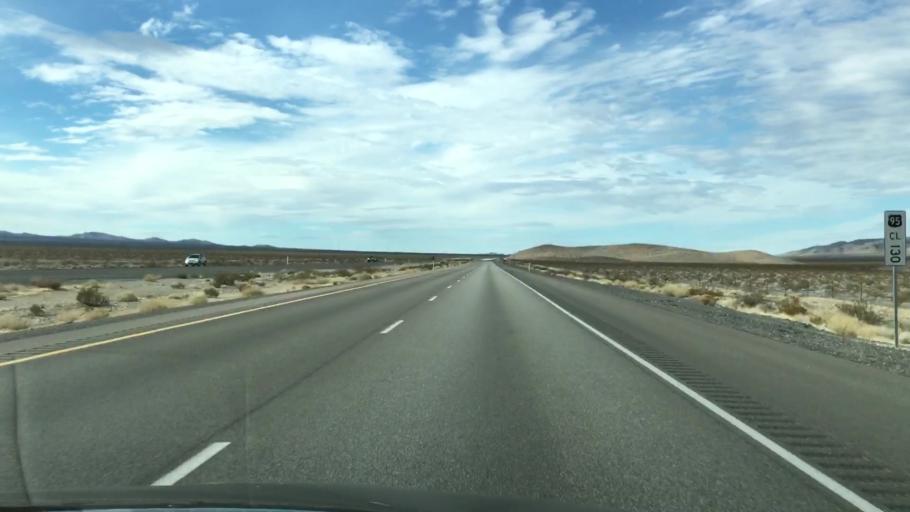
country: US
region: Nevada
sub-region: Nye County
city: Pahrump
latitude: 36.5725
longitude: -115.8591
